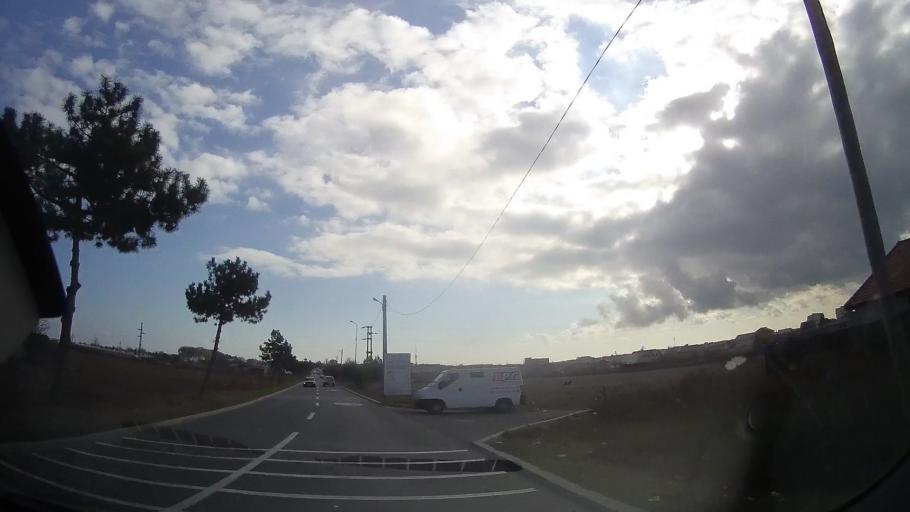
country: RO
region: Constanta
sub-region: Oras Techirghiol
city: Techirghiol
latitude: 44.0651
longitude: 28.5937
